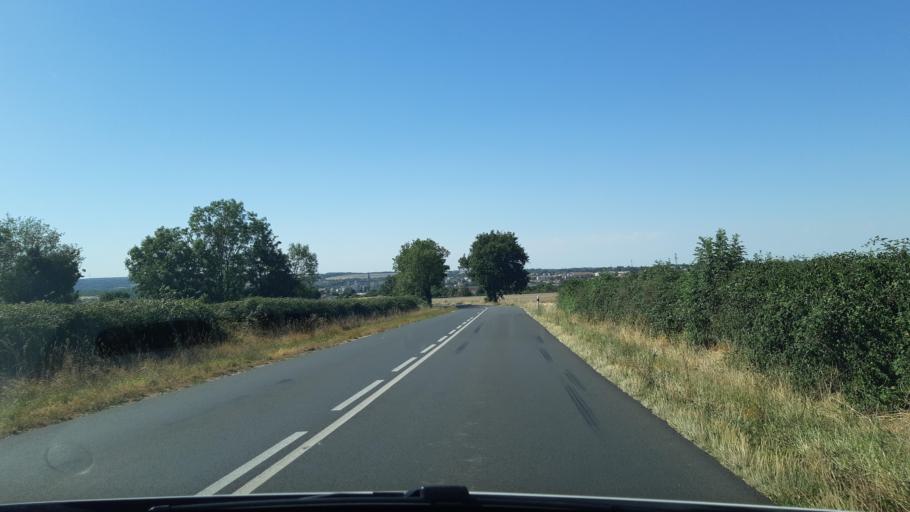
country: FR
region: Poitou-Charentes
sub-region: Departement des Deux-Sevres
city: Exireuil
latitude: 46.4360
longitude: -0.2041
